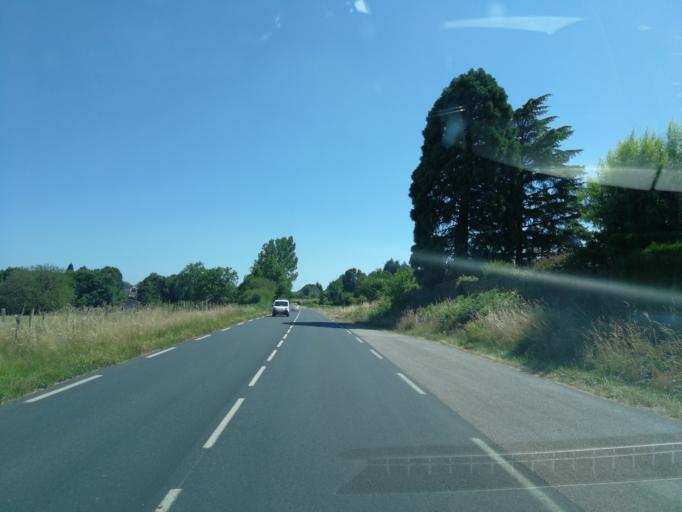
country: FR
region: Limousin
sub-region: Departement de la Correze
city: Sainte-Fereole
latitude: 45.2250
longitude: 1.5846
